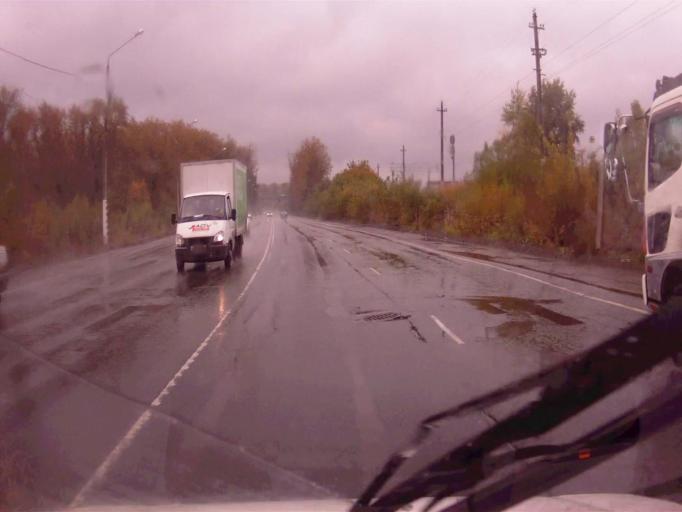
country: RU
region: Chelyabinsk
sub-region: Gorod Chelyabinsk
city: Chelyabinsk
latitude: 55.1983
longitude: 61.3945
